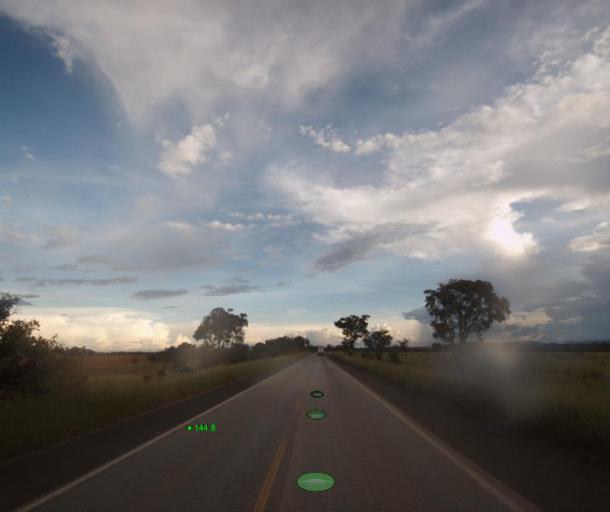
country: BR
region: Goias
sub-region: Uruacu
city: Uruacu
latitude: -14.0404
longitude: -49.0884
